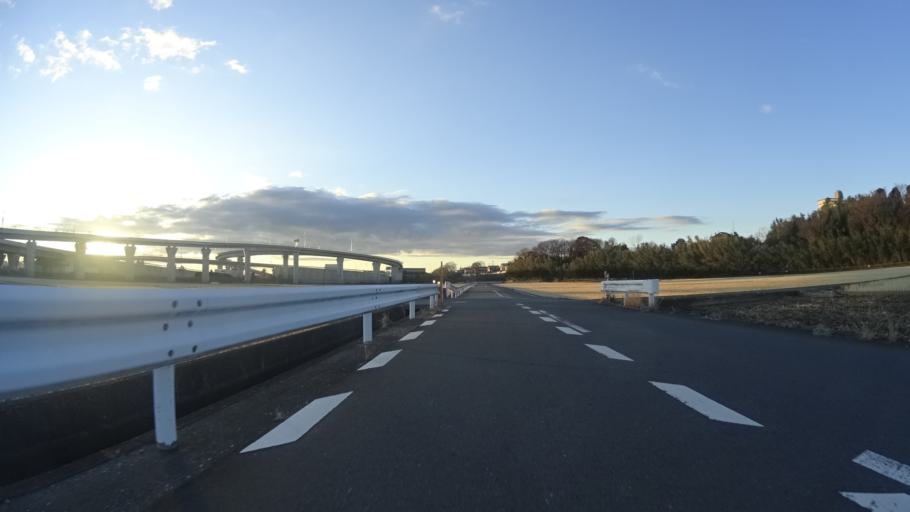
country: JP
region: Kanagawa
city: Zama
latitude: 35.4822
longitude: 139.3705
